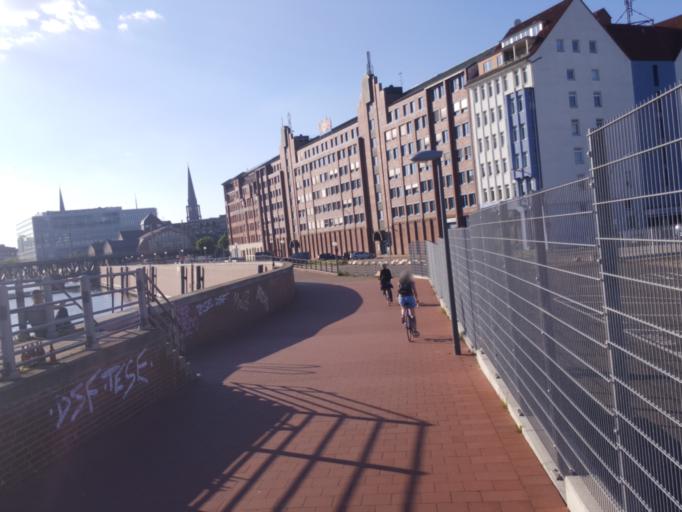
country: DE
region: Hamburg
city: Hamburg-Mitte
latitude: 53.5443
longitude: 10.0101
